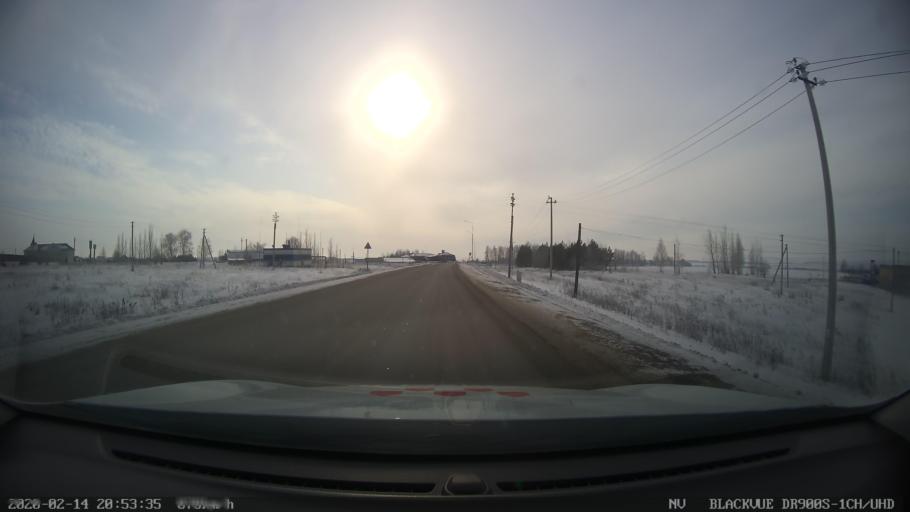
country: RU
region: Tatarstan
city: Kuybyshevskiy Zaton
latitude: 55.1930
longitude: 49.2474
